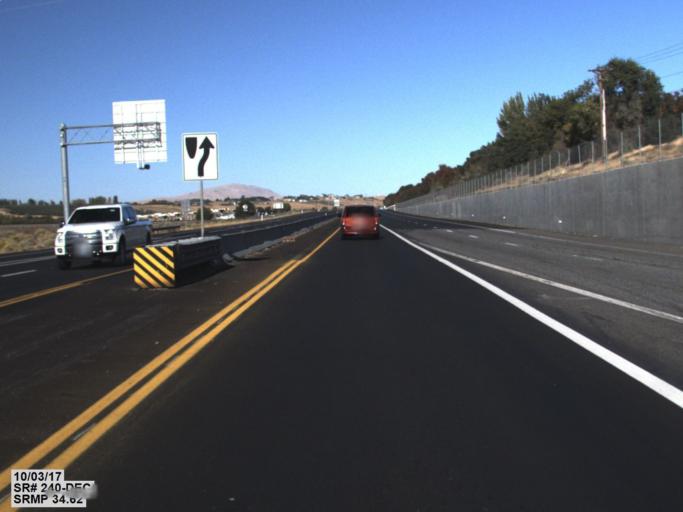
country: US
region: Washington
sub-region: Benton County
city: Richland
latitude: 46.2609
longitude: -119.2900
